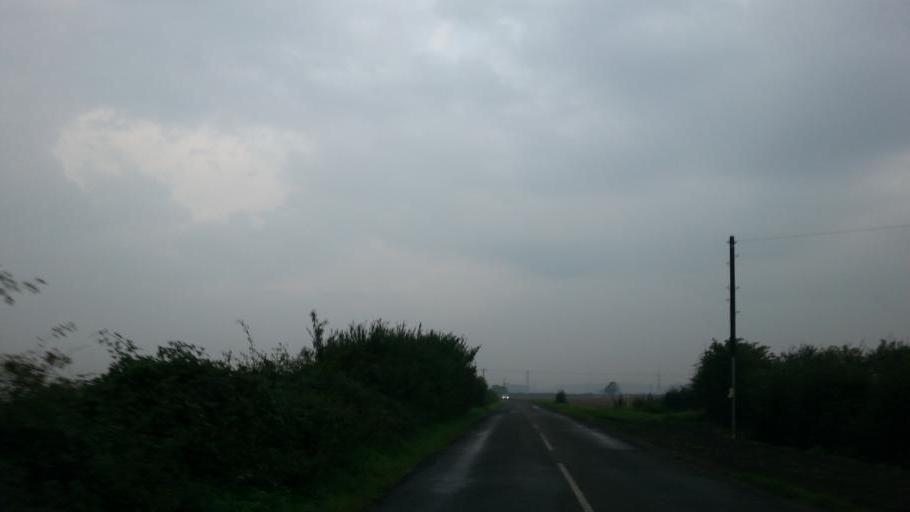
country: GB
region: England
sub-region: Nottinghamshire
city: Farndon
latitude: 53.0071
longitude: -0.8406
